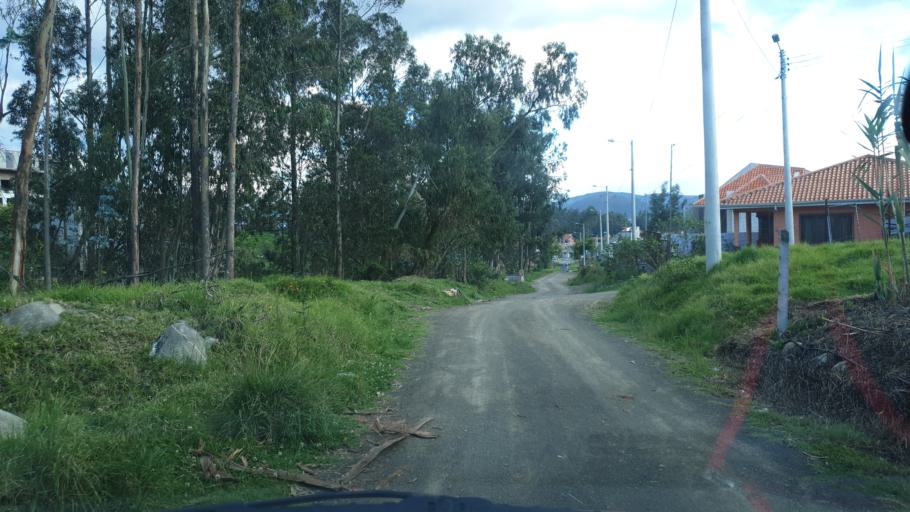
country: EC
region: Azuay
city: Cuenca
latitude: -2.8833
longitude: -79.0407
